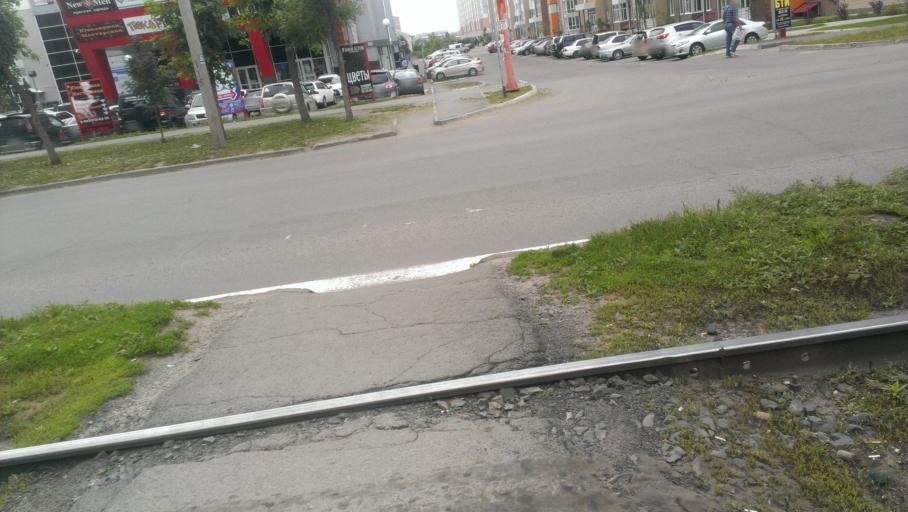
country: RU
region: Altai Krai
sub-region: Gorod Barnaulskiy
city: Barnaul
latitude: 53.3601
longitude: 83.6961
